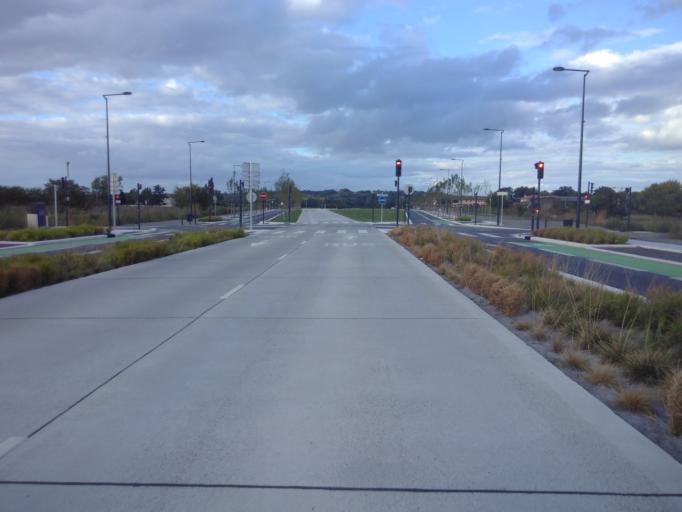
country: FR
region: Midi-Pyrenees
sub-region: Departement de la Haute-Garonne
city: Launaguet
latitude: 43.6517
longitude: 1.4575
